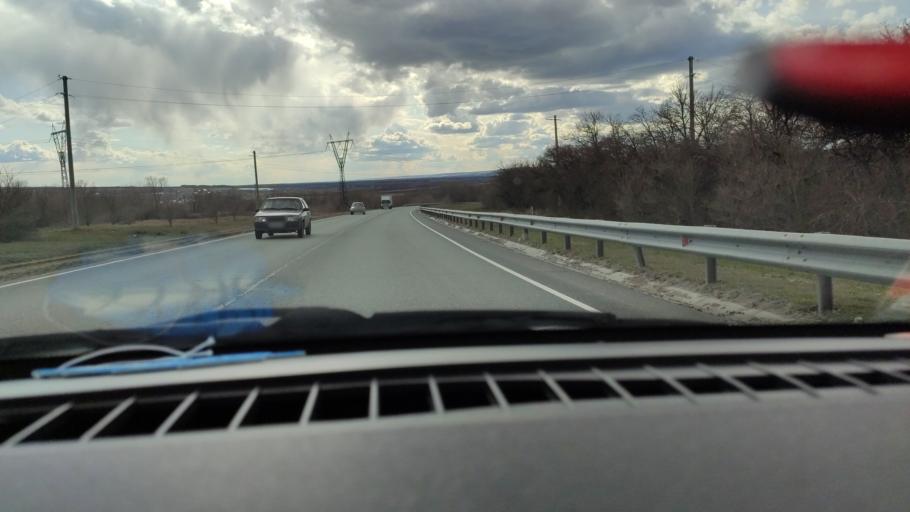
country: RU
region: Saratov
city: Tersa
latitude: 52.0829
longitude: 47.6663
